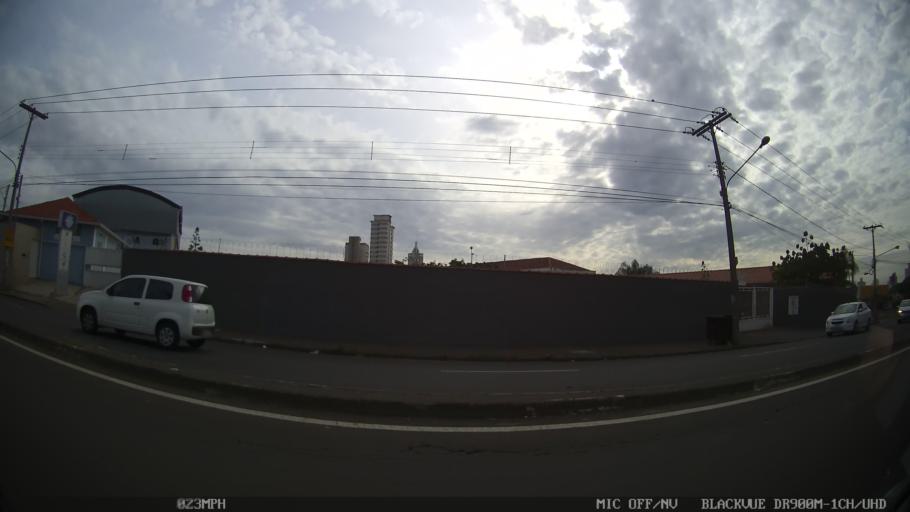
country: BR
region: Sao Paulo
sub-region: Piracicaba
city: Piracicaba
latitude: -22.7391
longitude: -47.6409
